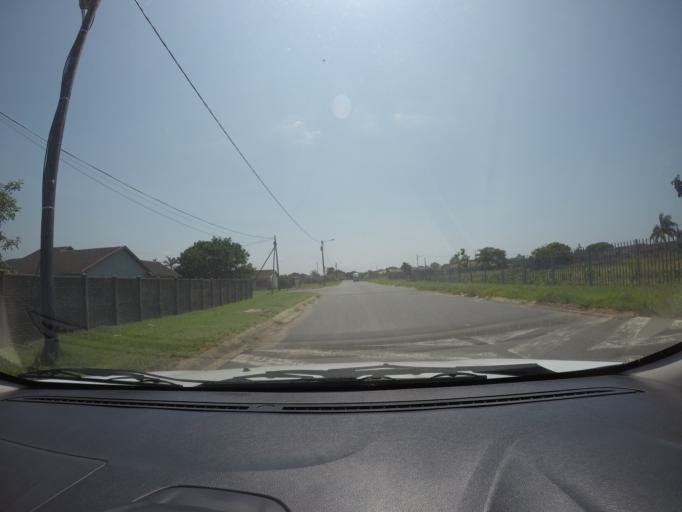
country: ZA
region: KwaZulu-Natal
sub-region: uThungulu District Municipality
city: eSikhawini
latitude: -28.8648
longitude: 31.9234
